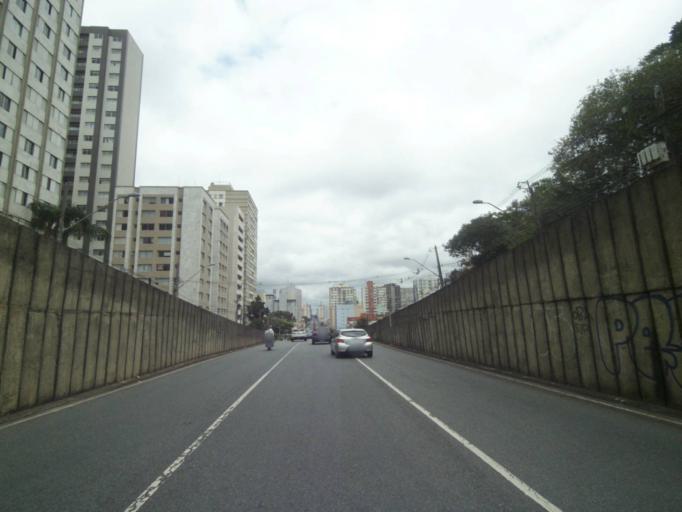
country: BR
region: Parana
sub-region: Curitiba
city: Curitiba
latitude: -25.4321
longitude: -49.2569
